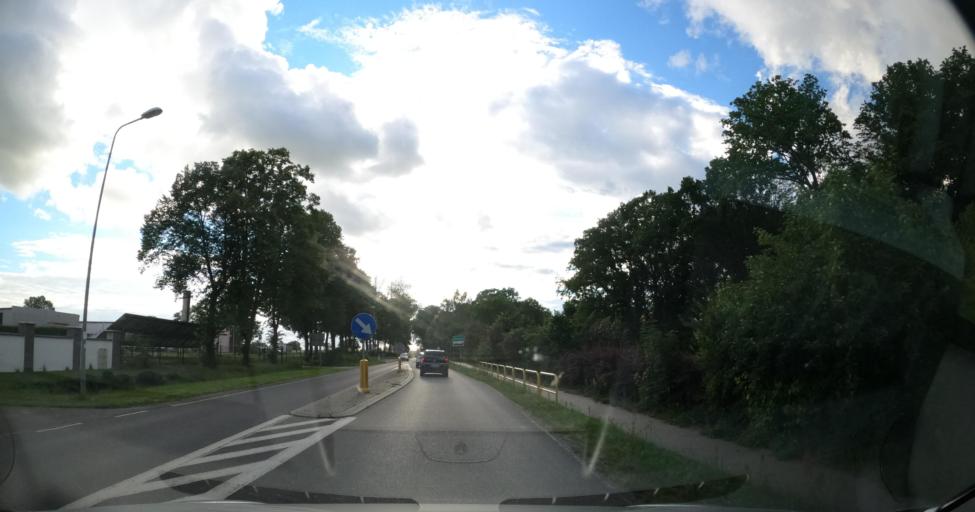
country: PL
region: Pomeranian Voivodeship
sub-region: Powiat slupski
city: Potegowo
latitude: 54.4193
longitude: 17.3908
